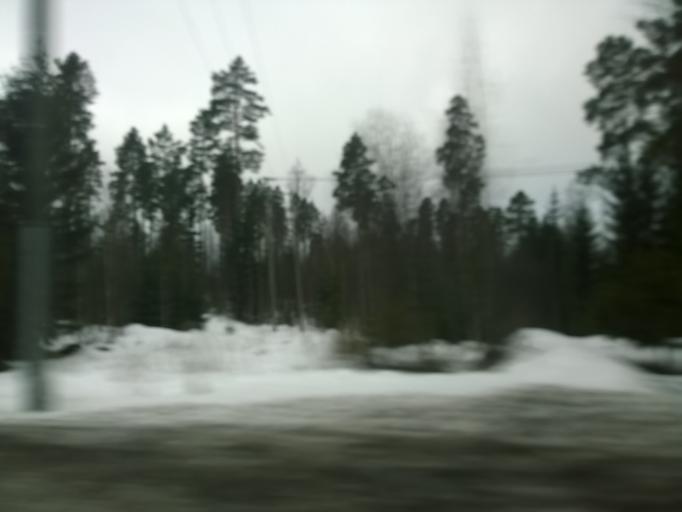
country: FI
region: Pirkanmaa
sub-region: Tampere
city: Lempaeaelae
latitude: 61.3963
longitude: 23.7730
